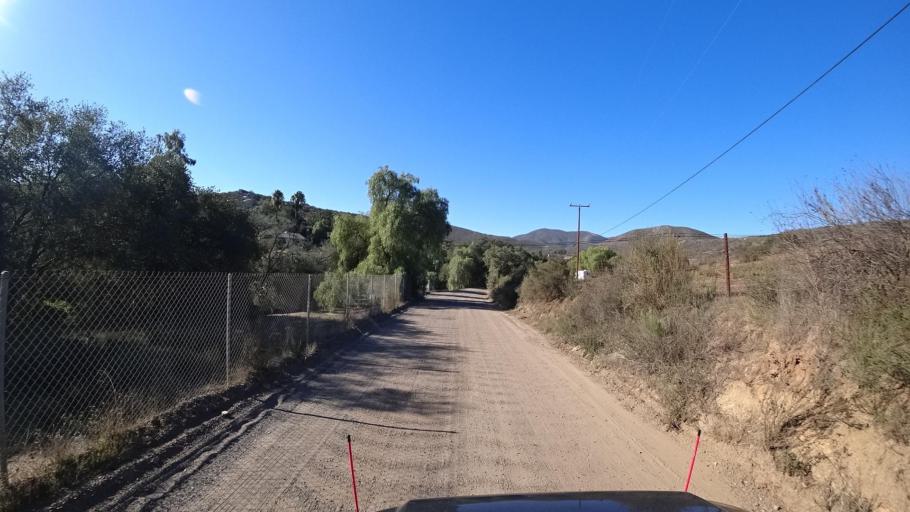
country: MX
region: Baja California
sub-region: Tijuana
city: El Nino
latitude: 32.6298
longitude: -116.7665
